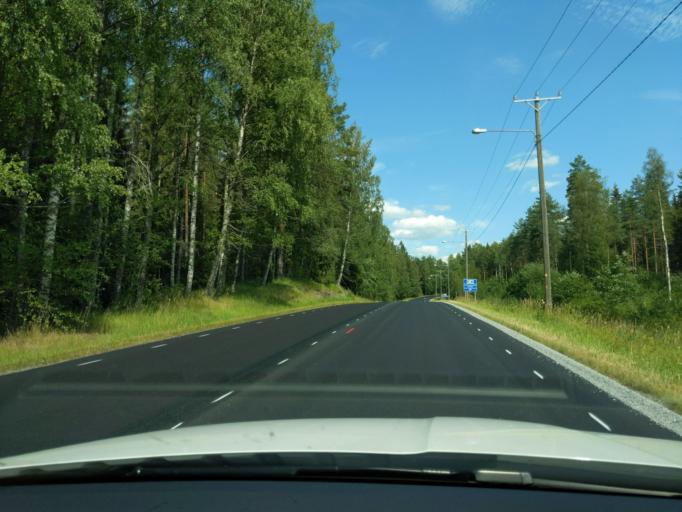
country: FI
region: Paijanne Tavastia
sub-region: Lahti
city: Lahti
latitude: 61.0481
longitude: 25.7712
